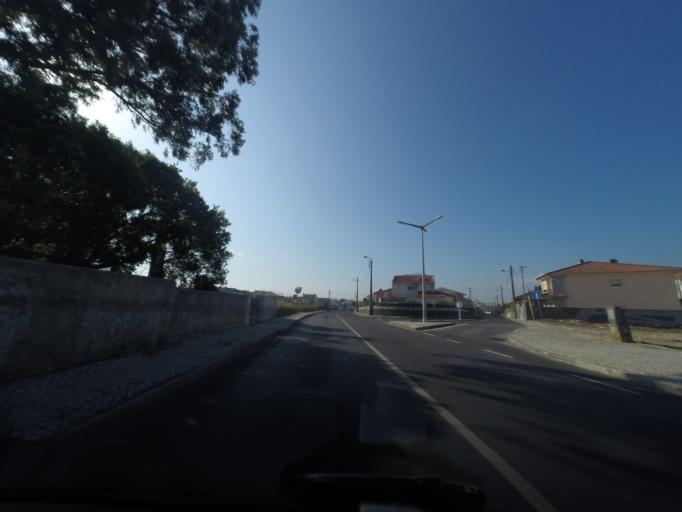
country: PT
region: Lisbon
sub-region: Cascais
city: Parede
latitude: 38.7216
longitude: -9.3498
